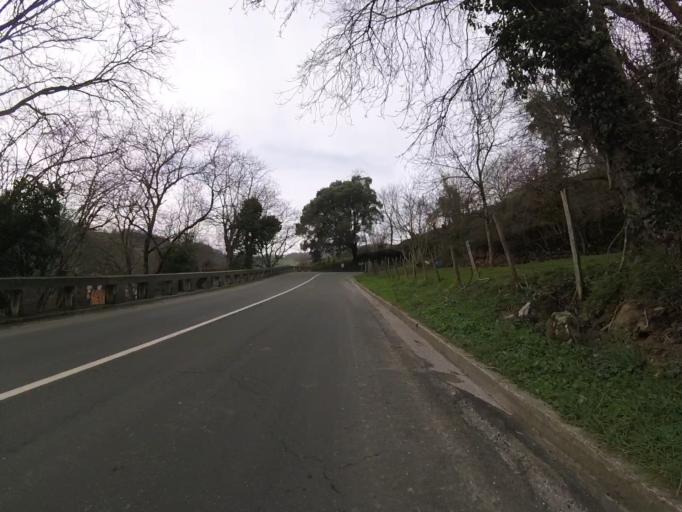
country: ES
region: Basque Country
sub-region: Provincia de Guipuzcoa
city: Errezil
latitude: 43.1425
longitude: -2.1699
